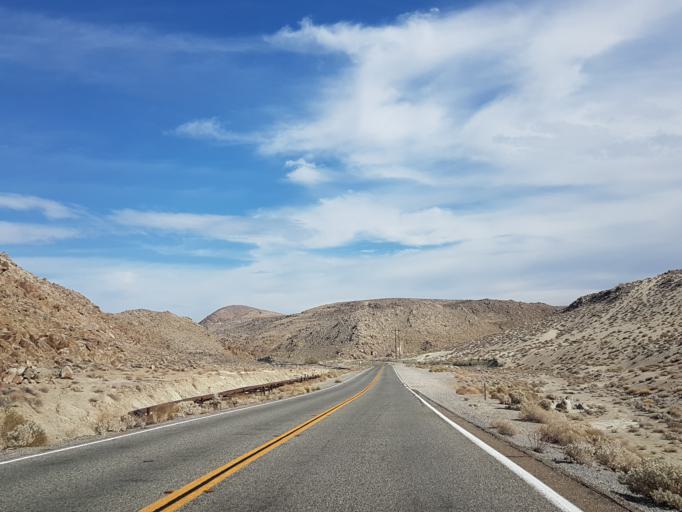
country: US
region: California
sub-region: San Bernardino County
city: Searles Valley
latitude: 35.6558
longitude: -117.4521
